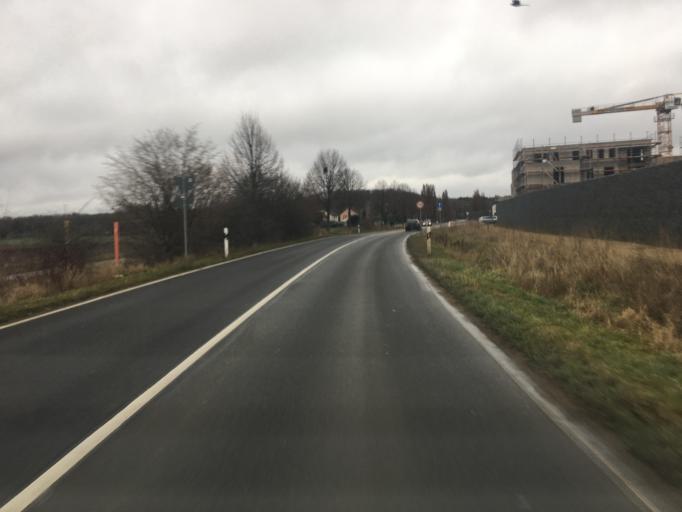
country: DE
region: North Rhine-Westphalia
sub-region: Regierungsbezirk Koln
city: Hurth
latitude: 50.8995
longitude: 6.8859
